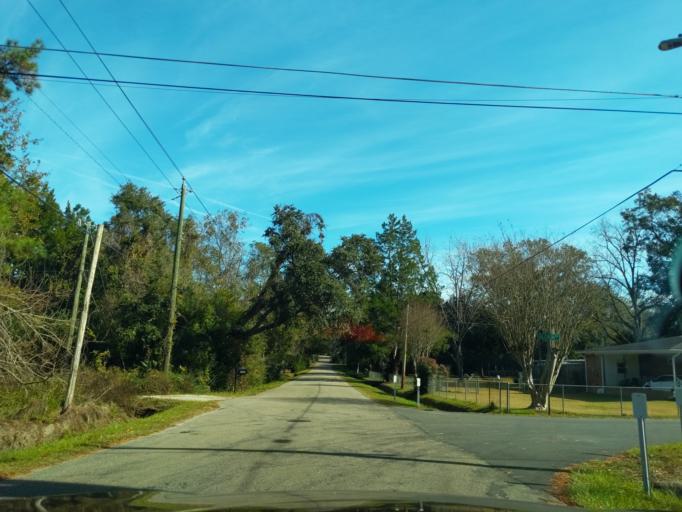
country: US
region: Florida
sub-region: Leon County
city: Tallahassee
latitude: 30.4695
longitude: -84.3380
